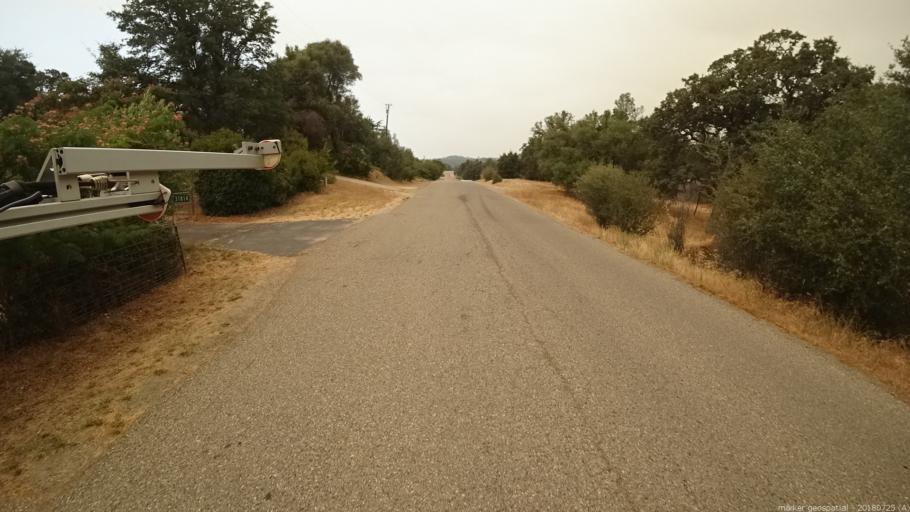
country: US
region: California
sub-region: Madera County
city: Coarsegold
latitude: 37.2111
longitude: -119.6788
